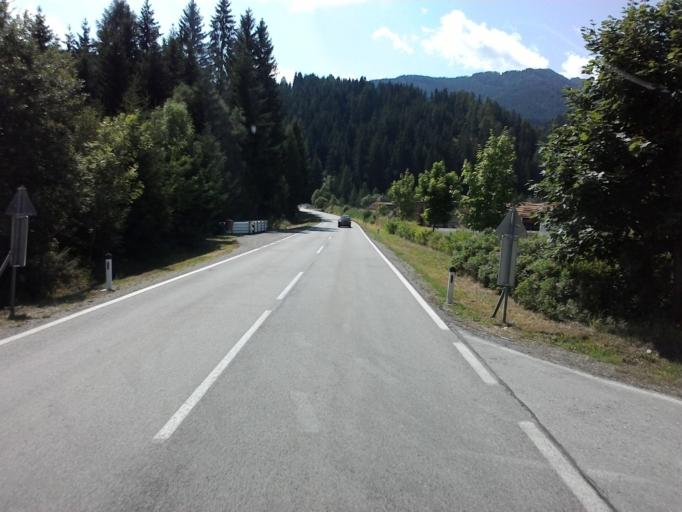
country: AT
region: Tyrol
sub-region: Politischer Bezirk Lienz
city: Heinfels
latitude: 46.7457
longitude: 12.4666
